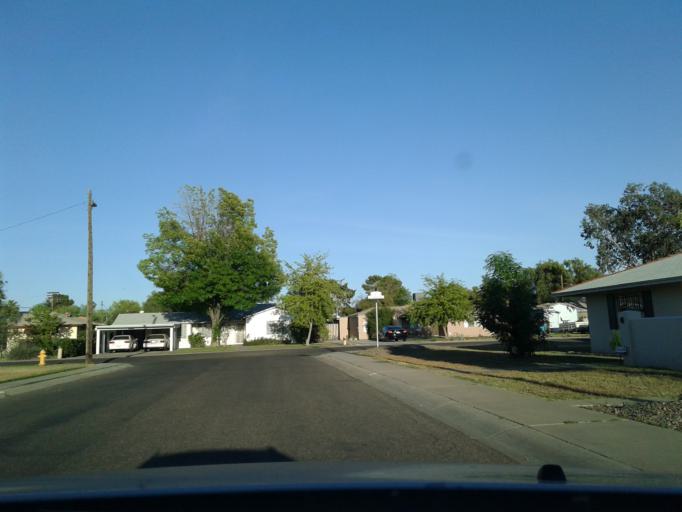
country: US
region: Arizona
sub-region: Maricopa County
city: Phoenix
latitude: 33.4992
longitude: -112.0951
